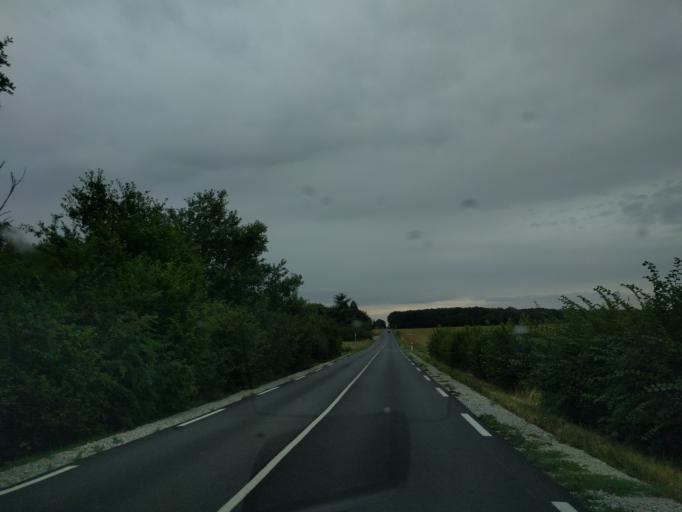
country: FR
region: Haute-Normandie
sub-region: Departement de l'Eure
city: Saint-Sebastien-de-Morsent
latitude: 49.0024
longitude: 1.0514
